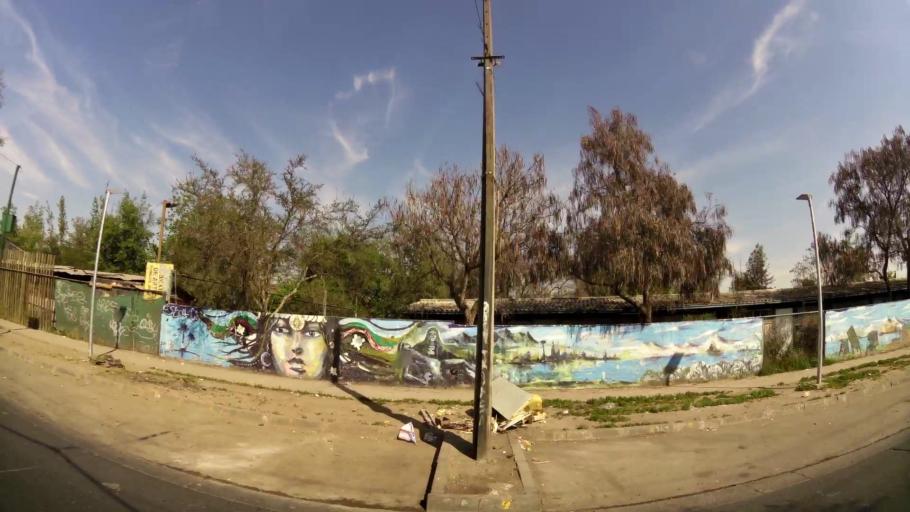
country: CL
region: Santiago Metropolitan
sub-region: Provincia de Santiago
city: La Pintana
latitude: -33.5582
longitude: -70.6618
